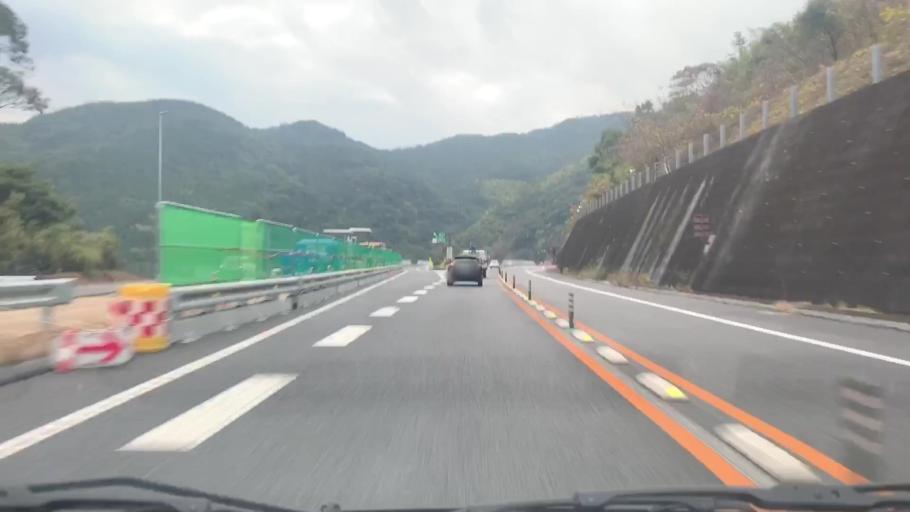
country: JP
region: Nagasaki
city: Nagasaki-shi
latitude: 32.7555
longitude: 129.9287
